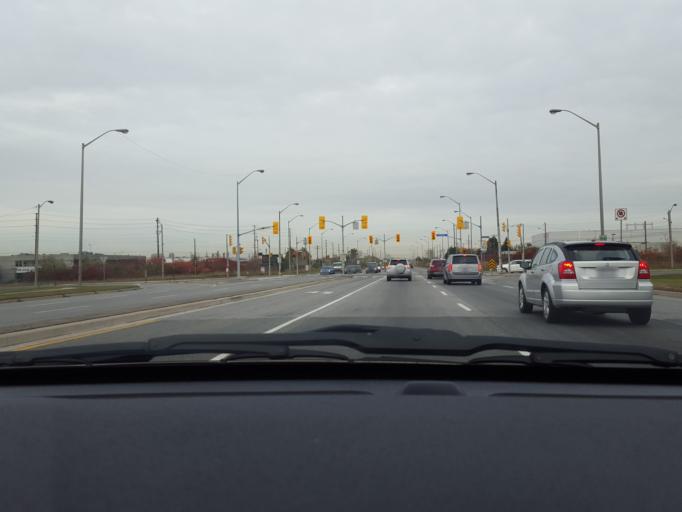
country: CA
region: Ontario
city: Etobicoke
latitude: 43.6985
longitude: -79.5867
